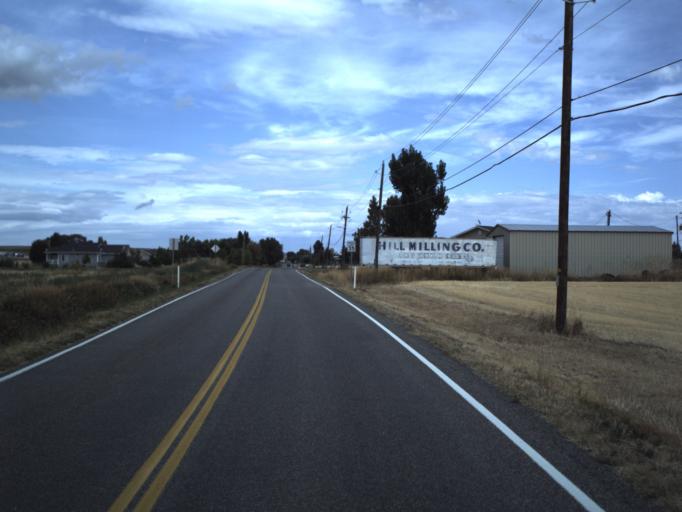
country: US
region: Utah
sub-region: Cache County
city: Benson
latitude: 41.8551
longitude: -112.0000
